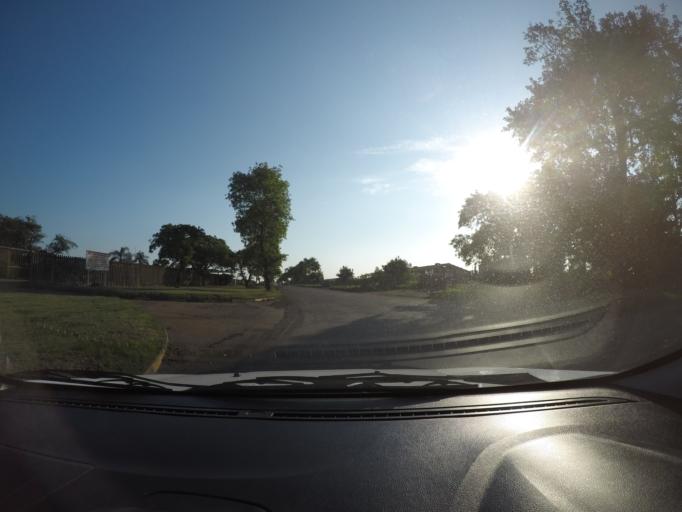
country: ZA
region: KwaZulu-Natal
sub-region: uThungulu District Municipality
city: Richards Bay
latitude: -28.7585
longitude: 32.0096
